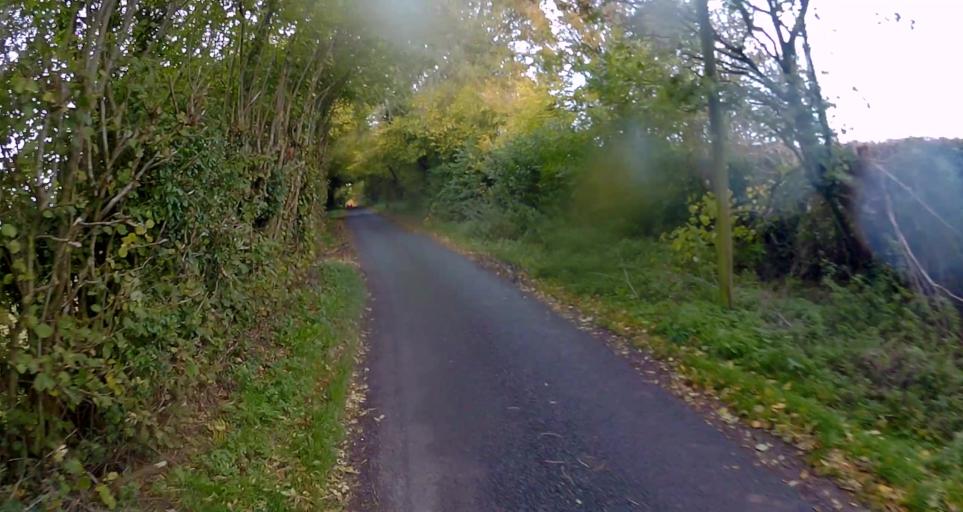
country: GB
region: England
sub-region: Hampshire
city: Four Marks
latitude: 51.1567
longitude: -1.0686
